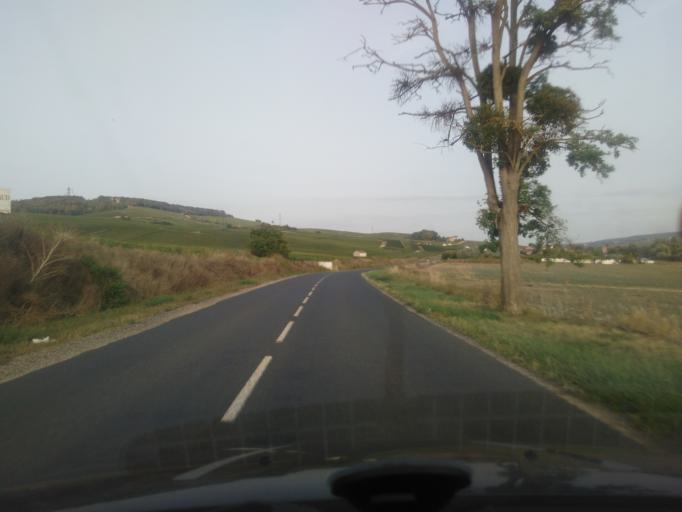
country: FR
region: Champagne-Ardenne
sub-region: Departement de la Marne
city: Mareuil-le-Port
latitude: 49.0869
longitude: 3.7872
